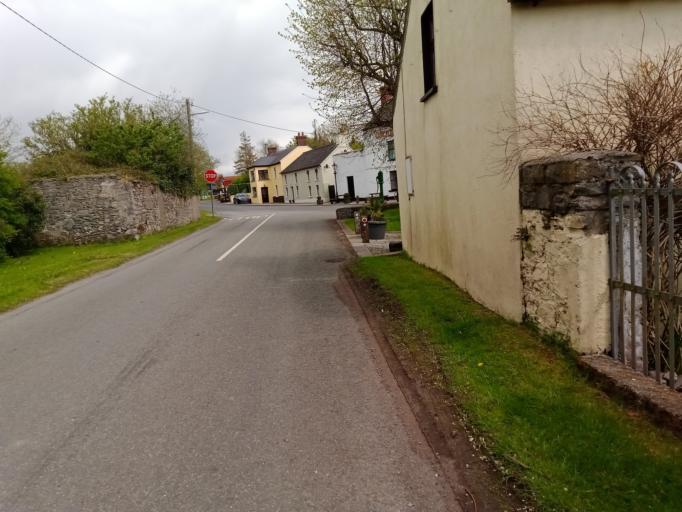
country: IE
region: Leinster
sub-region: Kilkenny
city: Kilkenny
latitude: 52.6009
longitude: -7.3050
